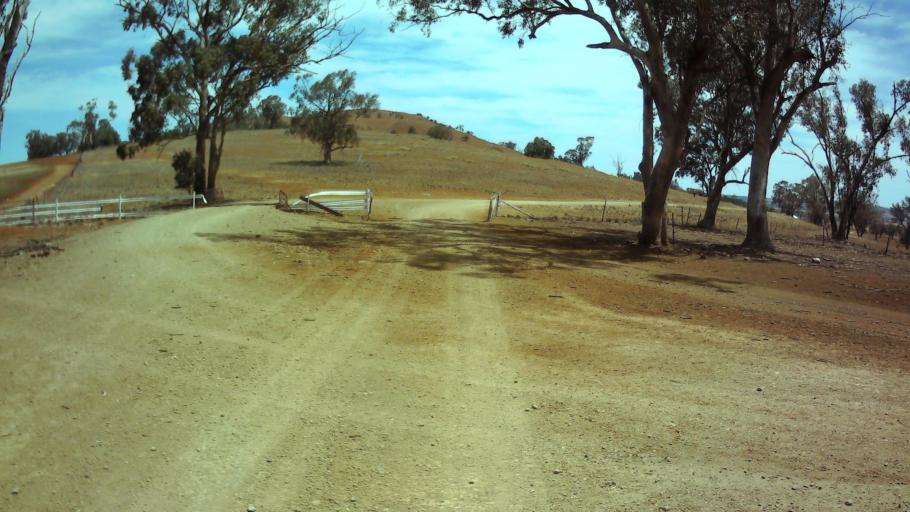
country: AU
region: New South Wales
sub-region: Weddin
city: Grenfell
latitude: -33.7473
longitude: 148.1688
